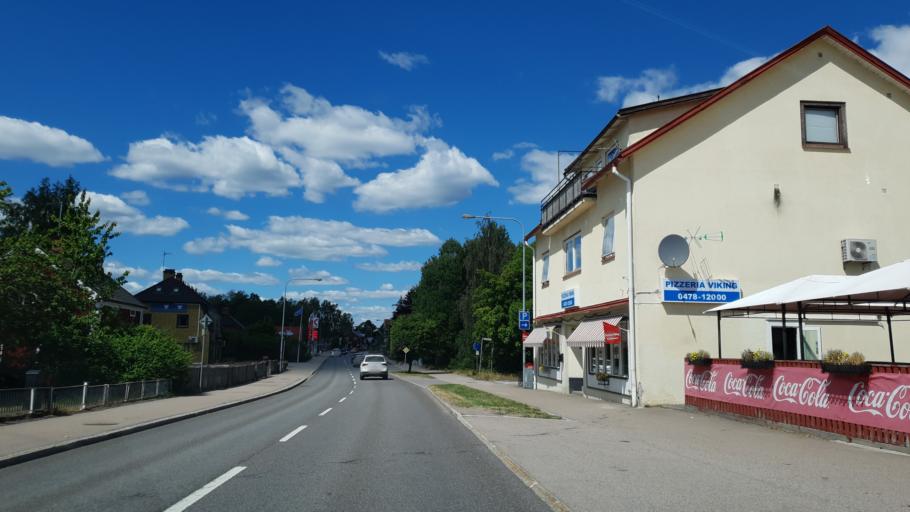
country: SE
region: Kronoberg
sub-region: Lessebo Kommun
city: Lessebo
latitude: 56.7531
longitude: 15.2691
